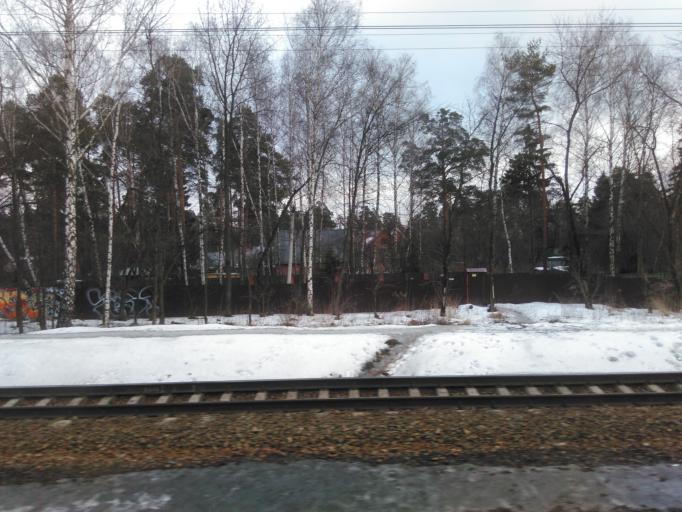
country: RU
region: Moskovskaya
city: Cherkizovo
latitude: 55.9383
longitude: 37.7892
